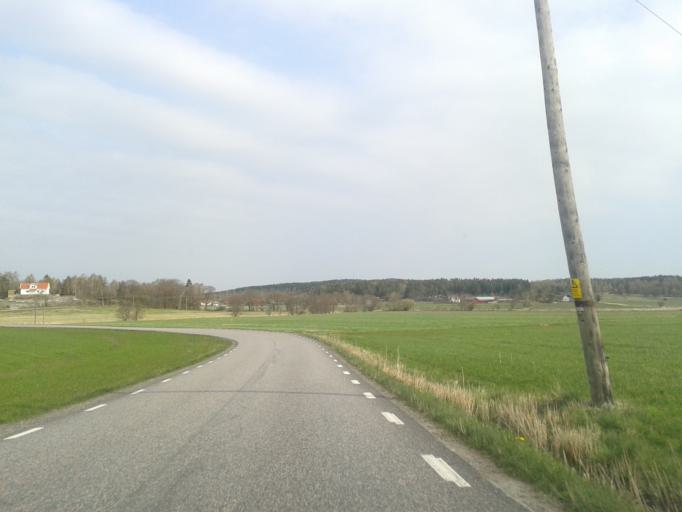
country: SE
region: Vaestra Goetaland
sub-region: Kungalvs Kommun
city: Kode
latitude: 57.9074
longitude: 11.8045
